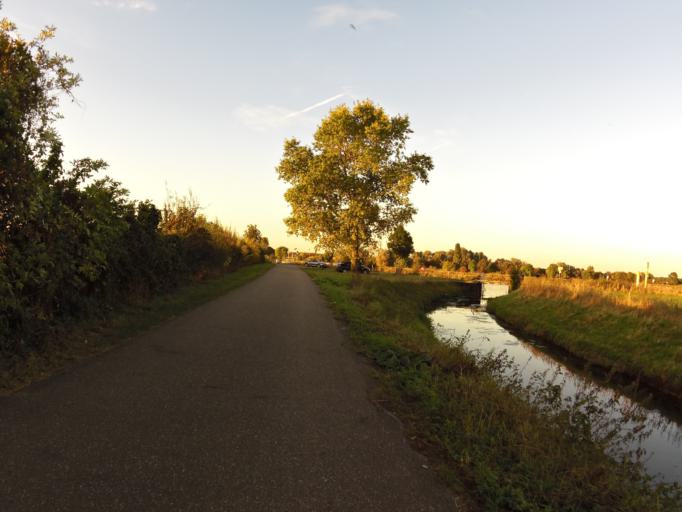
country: NL
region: North Brabant
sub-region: Gemeente Boxmeer
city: Boxmeer
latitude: 51.6413
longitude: 5.9749
